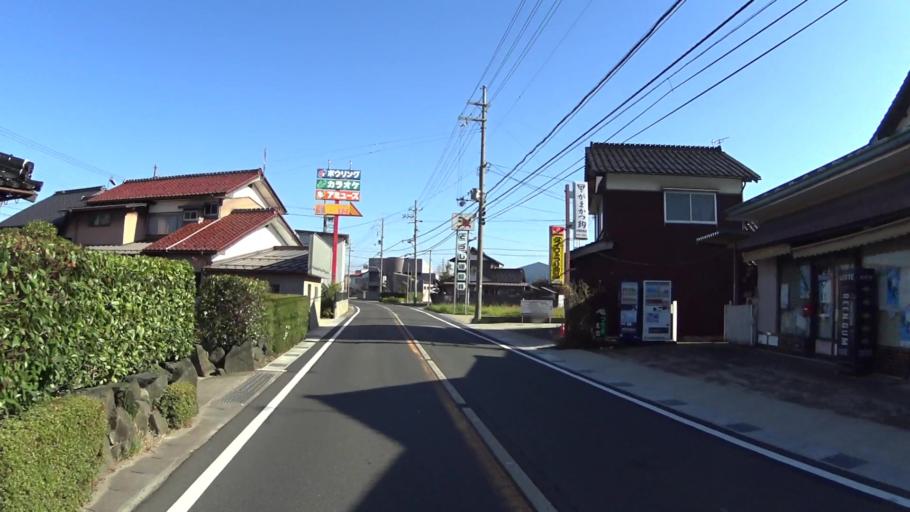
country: JP
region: Kyoto
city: Miyazu
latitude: 35.6129
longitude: 135.0638
